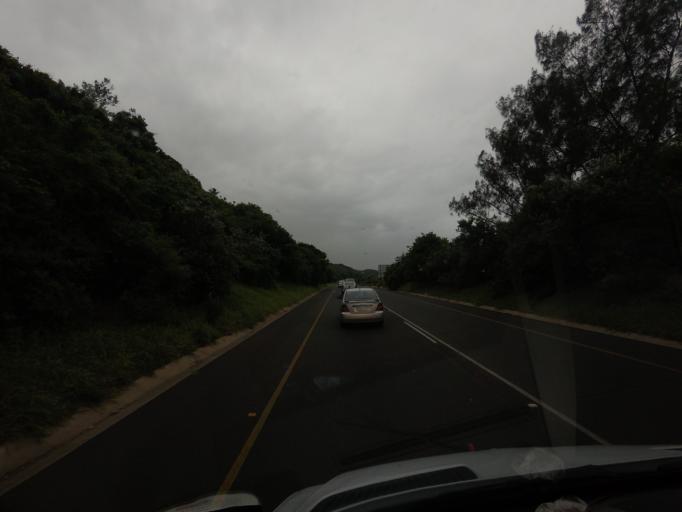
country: ZA
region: KwaZulu-Natal
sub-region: eThekwini Metropolitan Municipality
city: Durban
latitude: -29.7134
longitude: 31.0905
